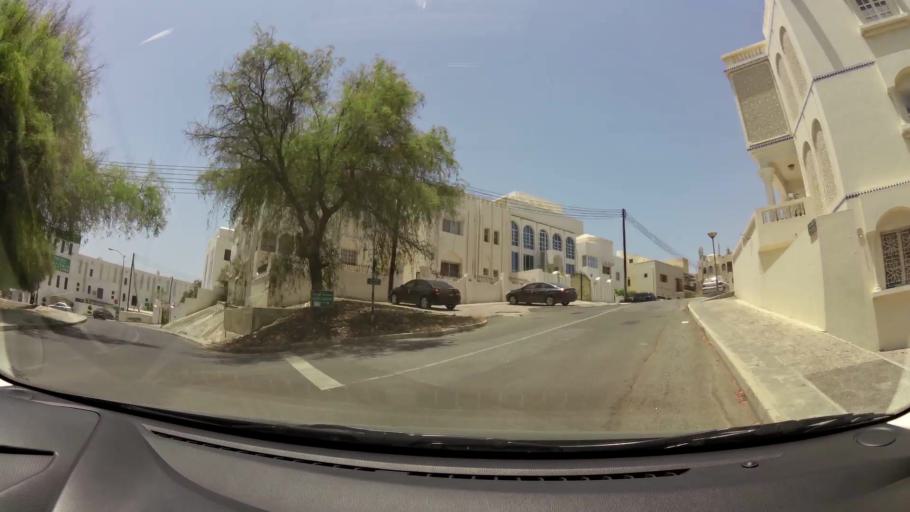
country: OM
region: Muhafazat Masqat
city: Muscat
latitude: 23.6228
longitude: 58.4925
